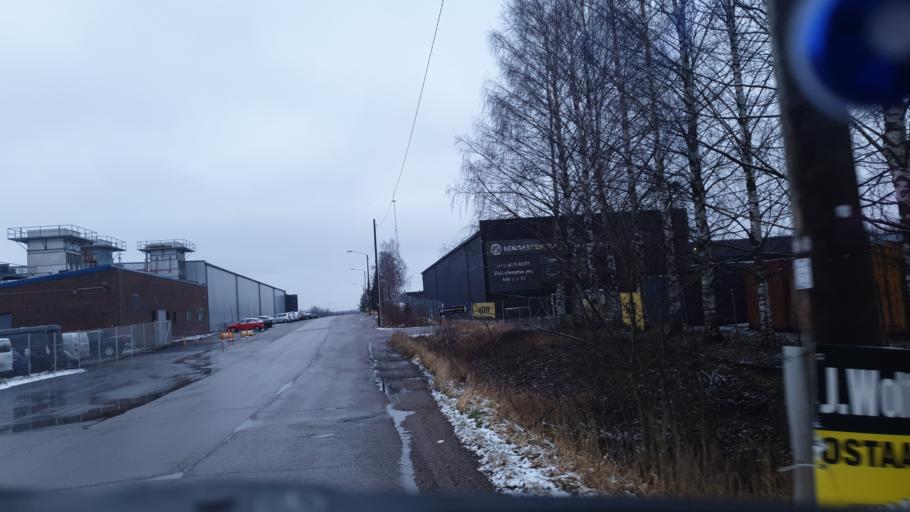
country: FI
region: Uusimaa
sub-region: Helsinki
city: Vantaa
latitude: 60.3234
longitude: 24.9137
